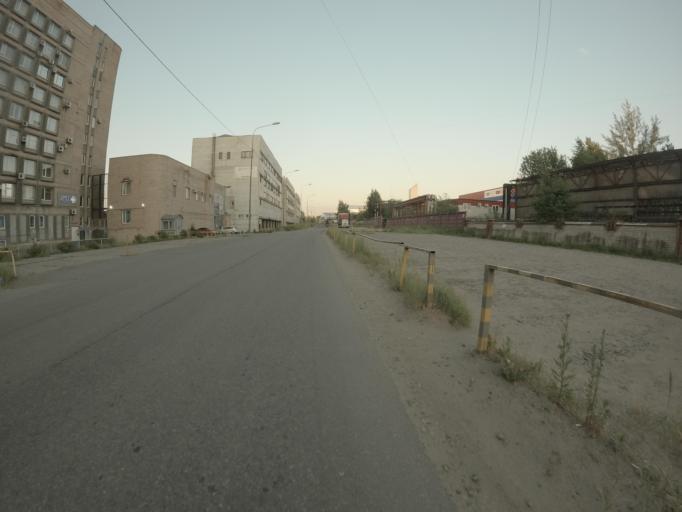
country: RU
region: St.-Petersburg
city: Admiralteisky
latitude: 59.8866
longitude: 30.2879
